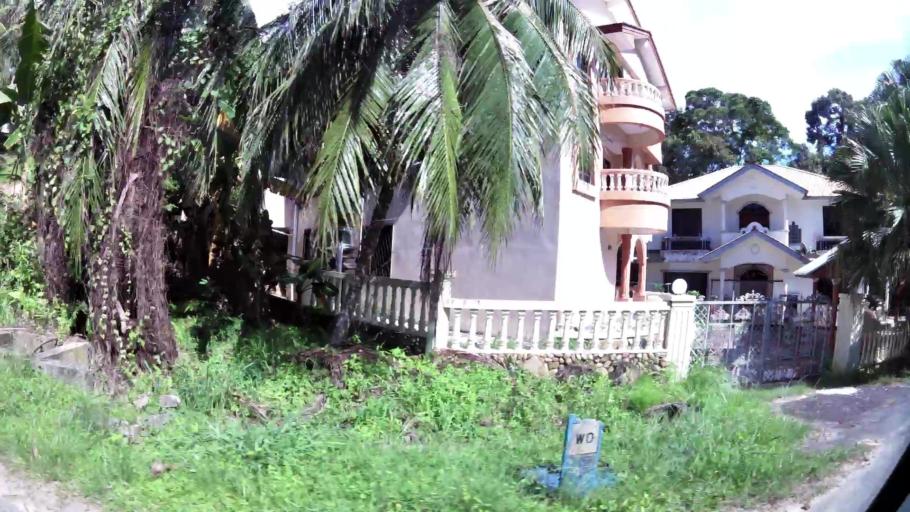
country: BN
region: Brunei and Muara
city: Bandar Seri Begawan
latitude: 5.0261
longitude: 115.0430
